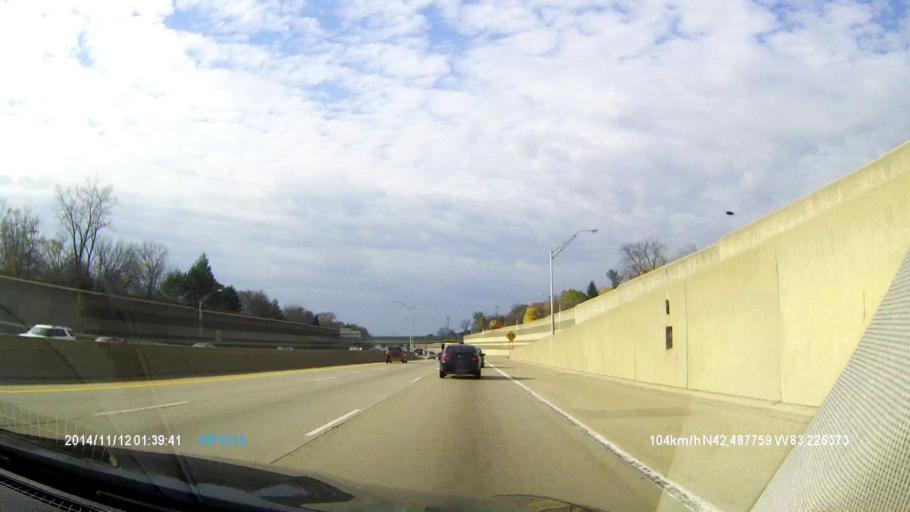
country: US
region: Michigan
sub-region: Oakland County
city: Lathrup Village
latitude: 42.4878
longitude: -83.2270
